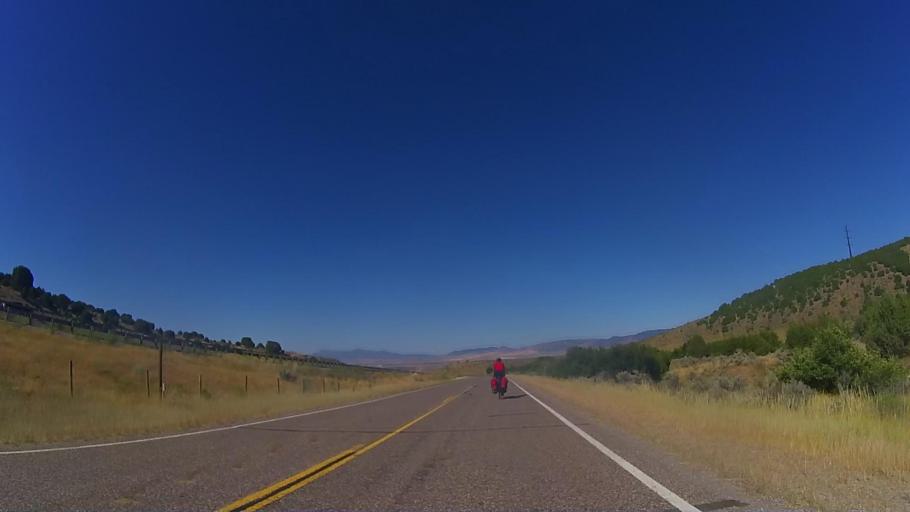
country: US
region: Idaho
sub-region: Oneida County
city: Malad City
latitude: 42.3644
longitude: -112.2143
